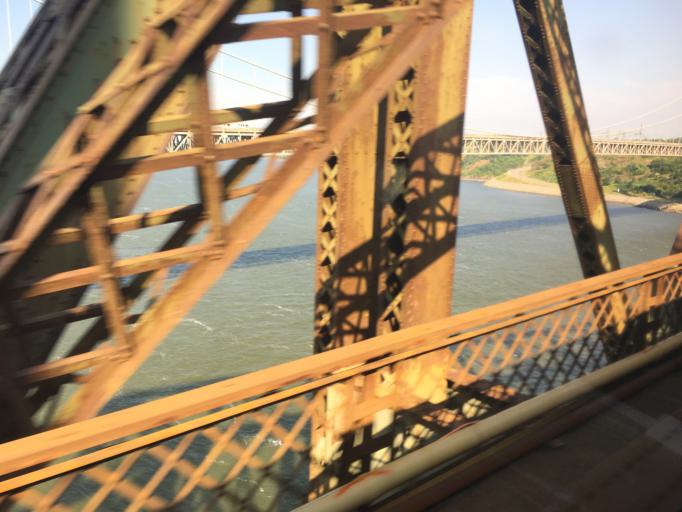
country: CA
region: Quebec
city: L'Ancienne-Lorette
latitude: 46.7436
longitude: -71.2869
